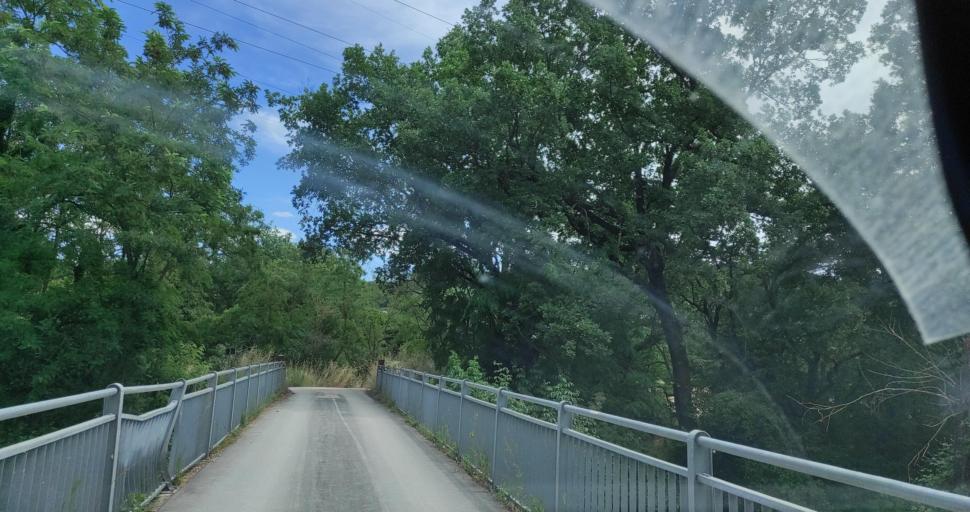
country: IT
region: The Marches
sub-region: Provincia di Macerata
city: Urbisaglia
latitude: 43.2070
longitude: 13.3955
